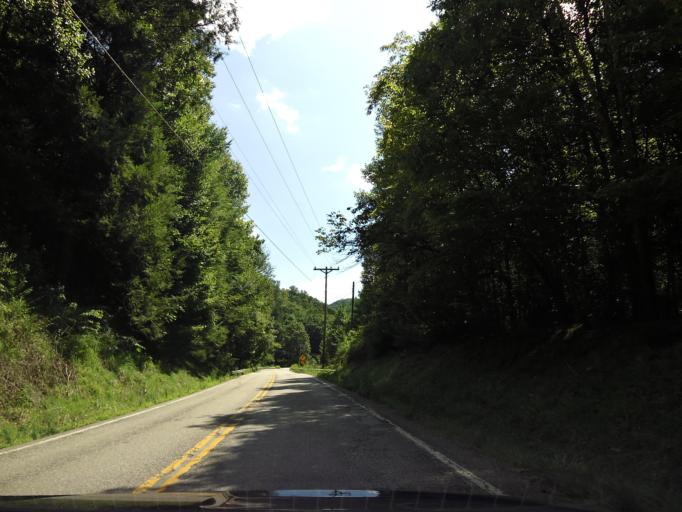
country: US
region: Kentucky
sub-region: Harlan County
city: Loyall
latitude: 36.9309
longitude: -83.3742
